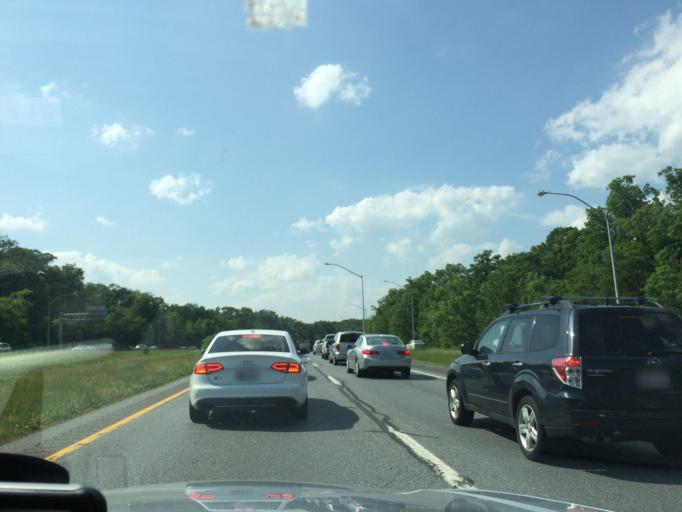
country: US
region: Maryland
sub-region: Howard County
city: Savage
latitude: 39.1423
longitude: -76.8177
